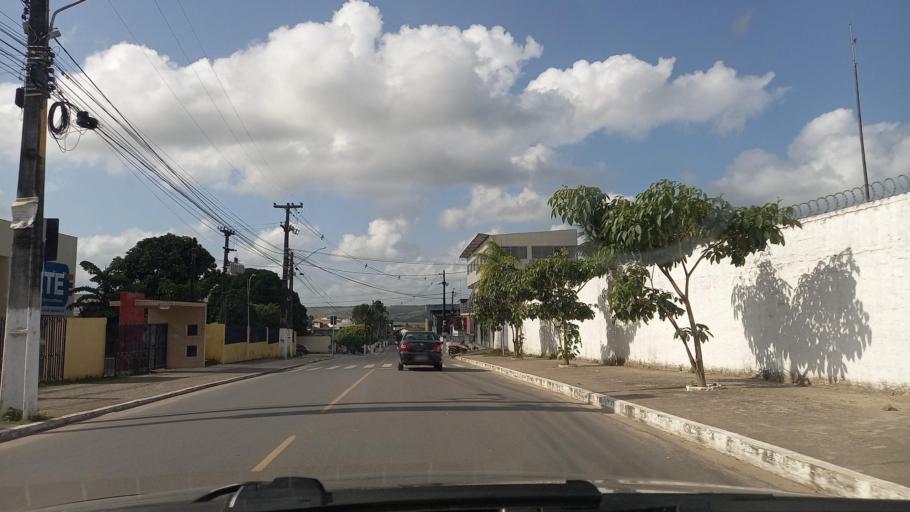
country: BR
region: Pernambuco
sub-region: Goiana
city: Goiana
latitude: -7.5619
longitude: -35.0125
